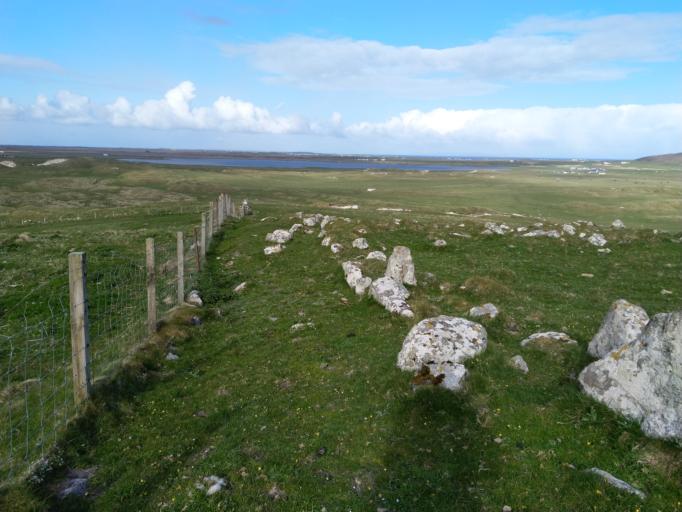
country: GB
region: Scotland
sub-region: Eilean Siar
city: Barra
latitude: 56.4624
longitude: -6.9677
